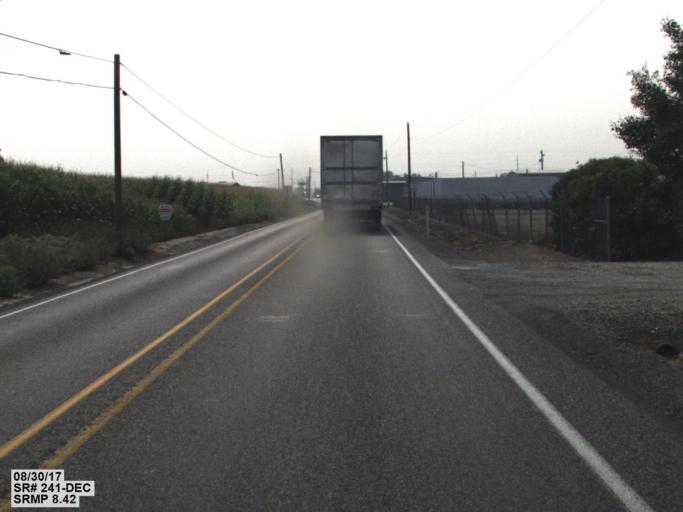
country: US
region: Washington
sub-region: Yakima County
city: Sunnyside
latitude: 46.3189
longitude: -119.9791
